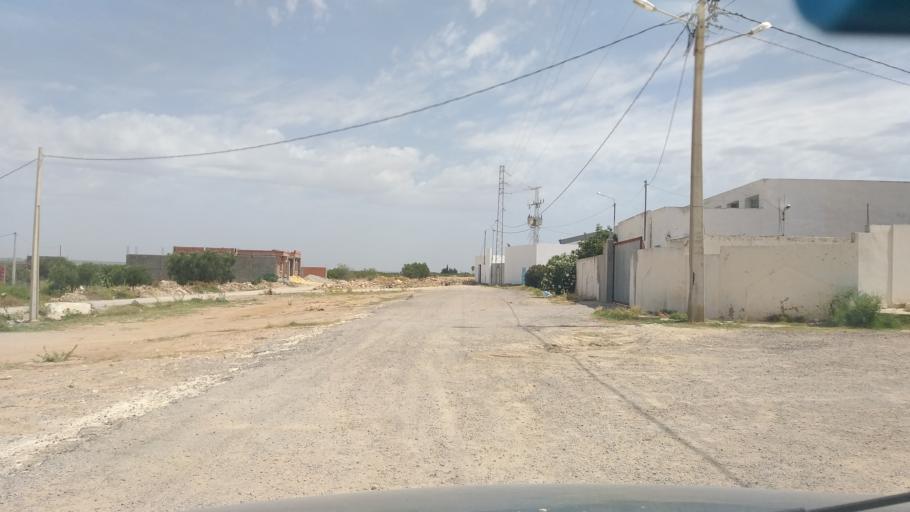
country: TN
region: Al Mahdiyah
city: El Jem
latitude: 35.3123
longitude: 10.7041
